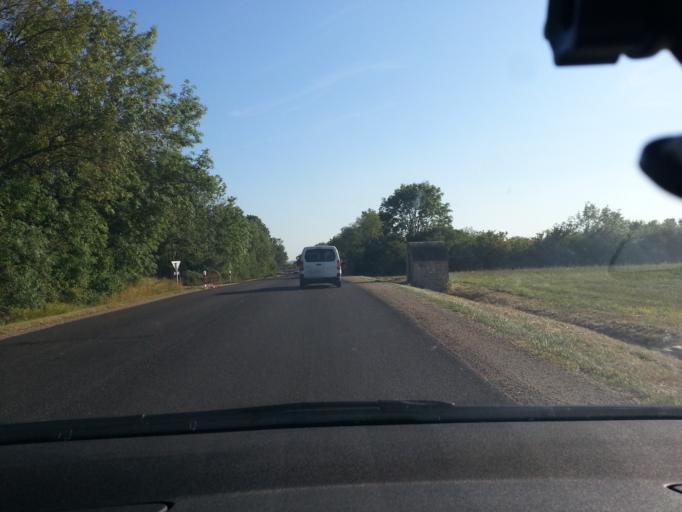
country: FR
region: Bourgogne
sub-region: Departement de la Cote-d'Or
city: Meursault
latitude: 46.9621
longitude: 4.7703
